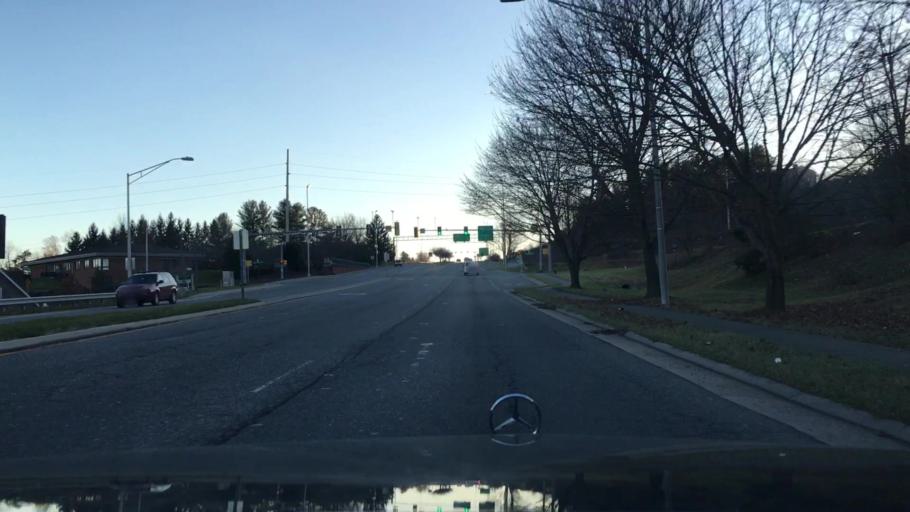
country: US
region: Virginia
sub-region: Montgomery County
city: Merrimac
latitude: 37.1987
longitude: -80.4010
